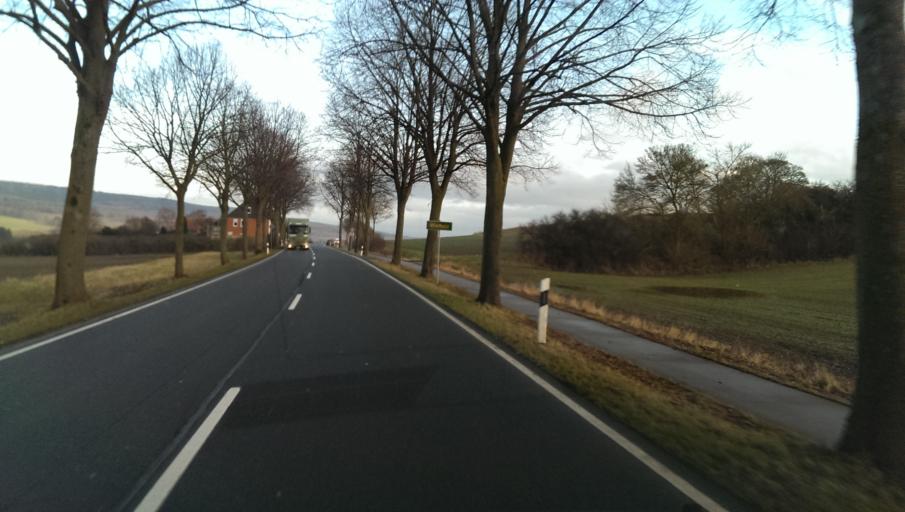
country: DE
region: Lower Saxony
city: Eimen
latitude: 51.8876
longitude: 9.7351
